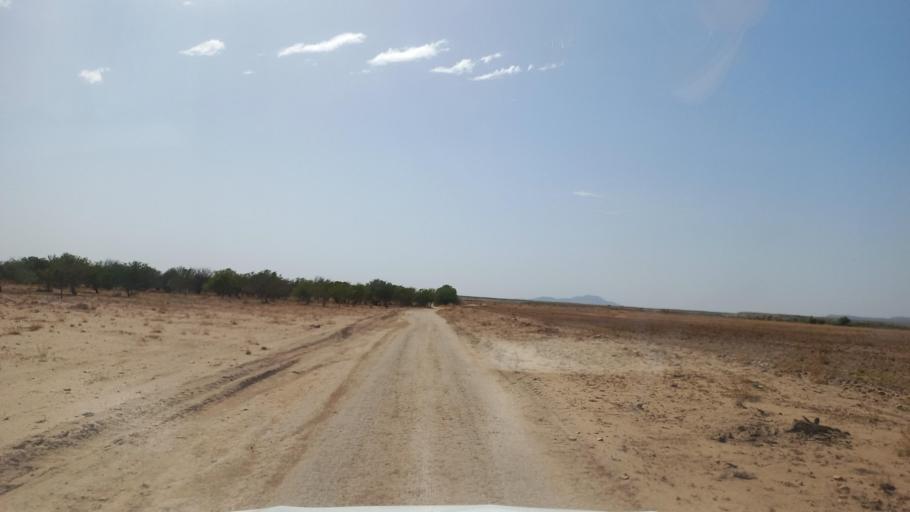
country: TN
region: Al Qasrayn
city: Kasserine
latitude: 35.2565
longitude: 8.9667
